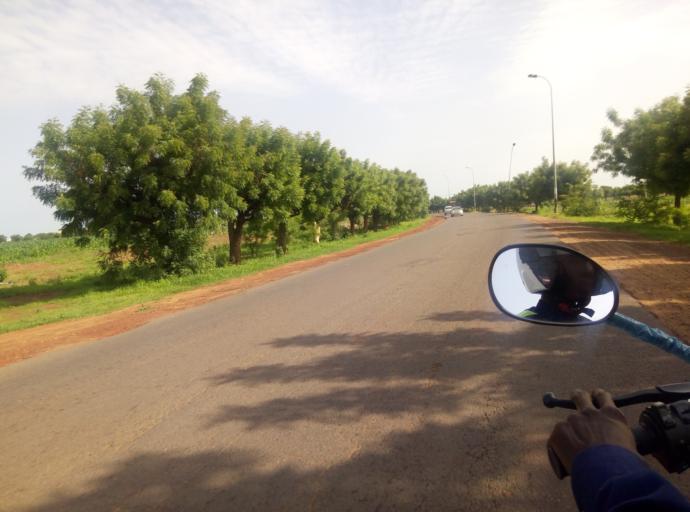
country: ML
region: Bamako
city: Bamako
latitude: 12.5498
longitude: -7.9510
